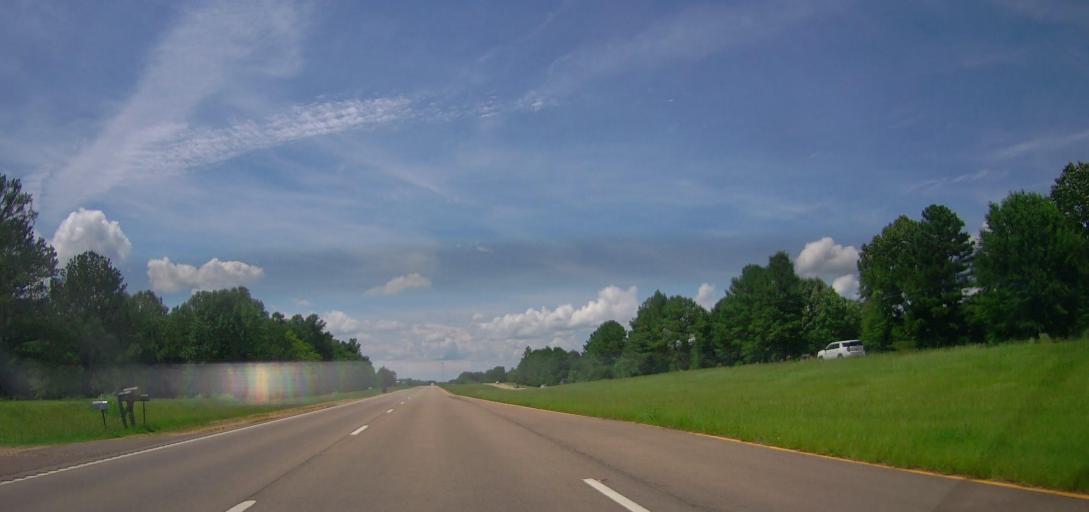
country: US
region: Mississippi
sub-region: Lee County
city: Nettleton
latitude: 33.9827
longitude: -88.6180
